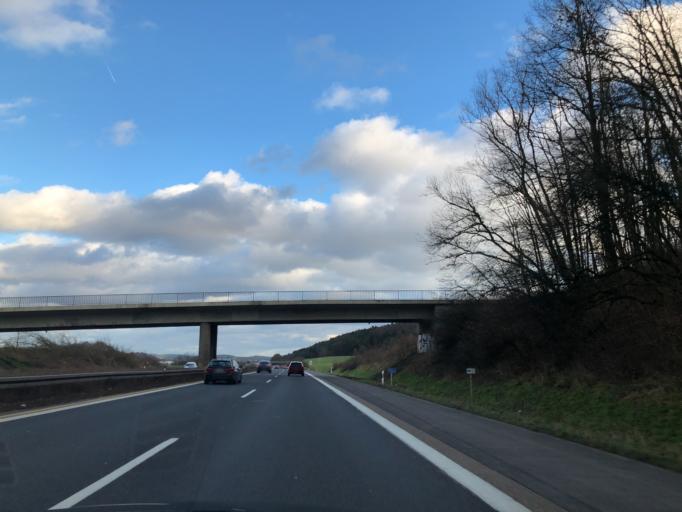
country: DE
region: Bavaria
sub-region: Regierungsbezirk Unterfranken
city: Geiselwind
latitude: 49.7637
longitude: 10.5226
